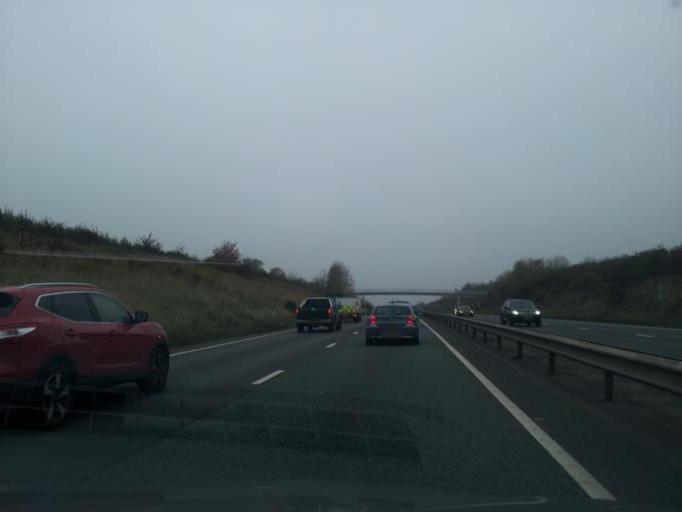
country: GB
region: England
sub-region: Leicestershire
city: Glenfield
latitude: 52.6576
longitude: -1.2133
